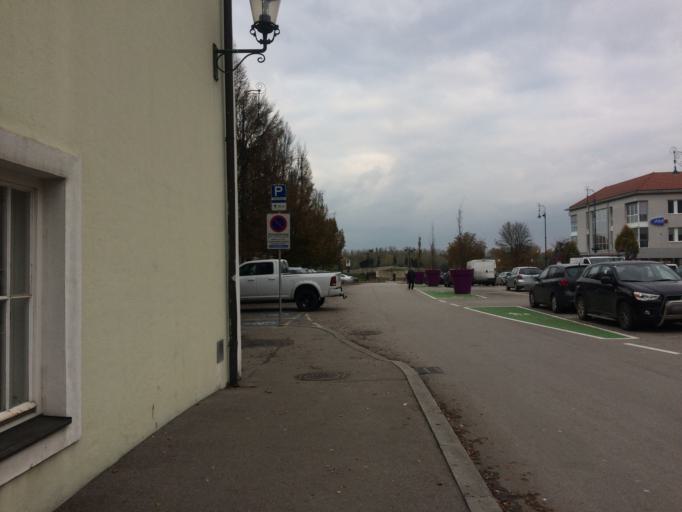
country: AT
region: Lower Austria
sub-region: Politischer Bezirk Tulln
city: Tulln
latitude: 48.3323
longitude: 16.0502
